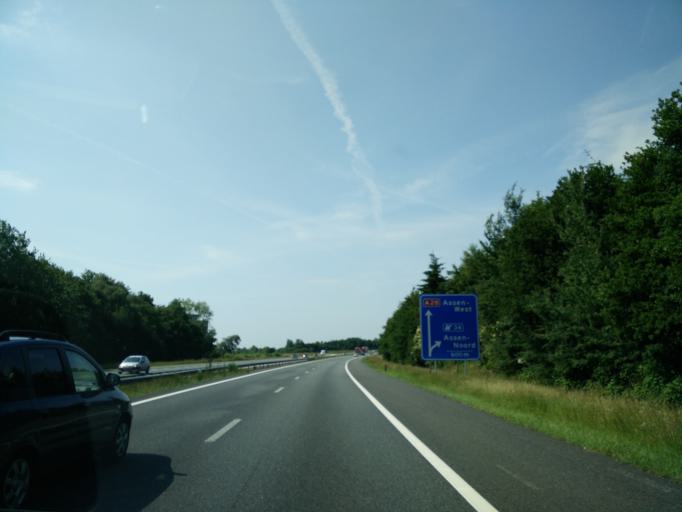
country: NL
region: Drenthe
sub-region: Gemeente Tynaarlo
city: Vries
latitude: 53.0343
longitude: 6.5795
